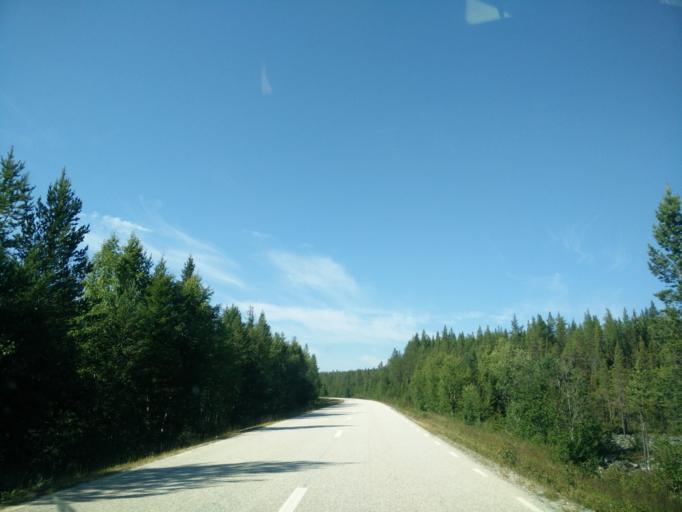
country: SE
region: Jaemtland
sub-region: Are Kommun
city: Jarpen
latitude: 62.8207
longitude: 13.5052
